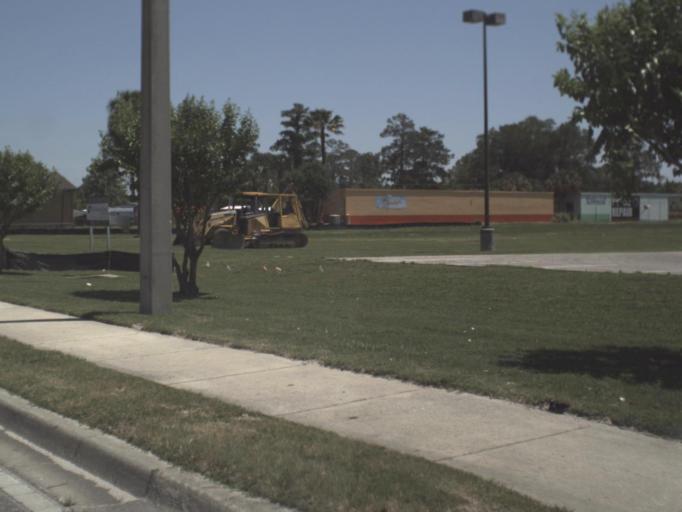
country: US
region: Florida
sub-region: Columbia County
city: Lake City
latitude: 30.1792
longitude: -82.6720
